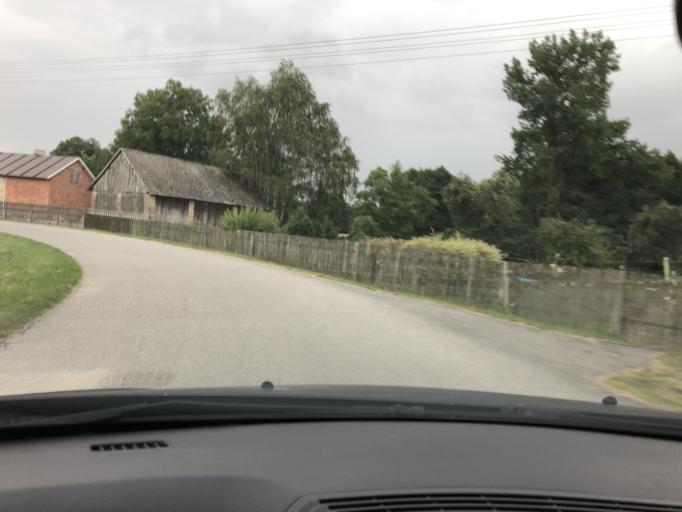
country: PL
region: Lodz Voivodeship
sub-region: Powiat wieruszowski
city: Czastary
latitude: 51.2427
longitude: 18.2766
